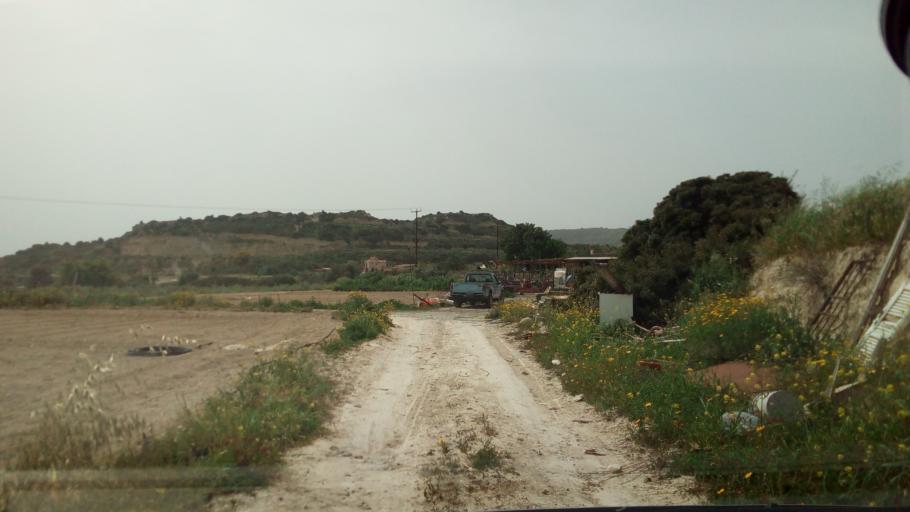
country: CY
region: Limassol
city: Pissouri
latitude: 34.6805
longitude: 32.7305
